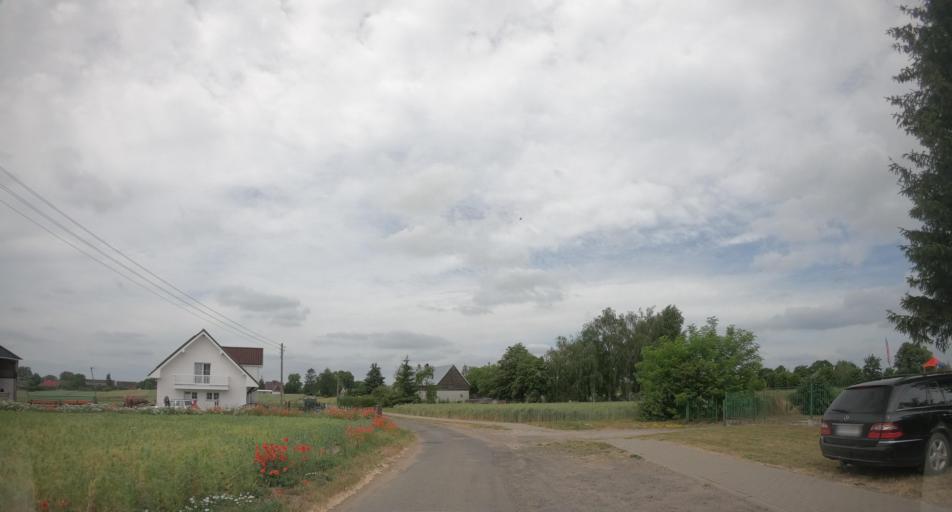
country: PL
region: West Pomeranian Voivodeship
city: Trzcinsko Zdroj
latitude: 52.9744
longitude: 14.6770
